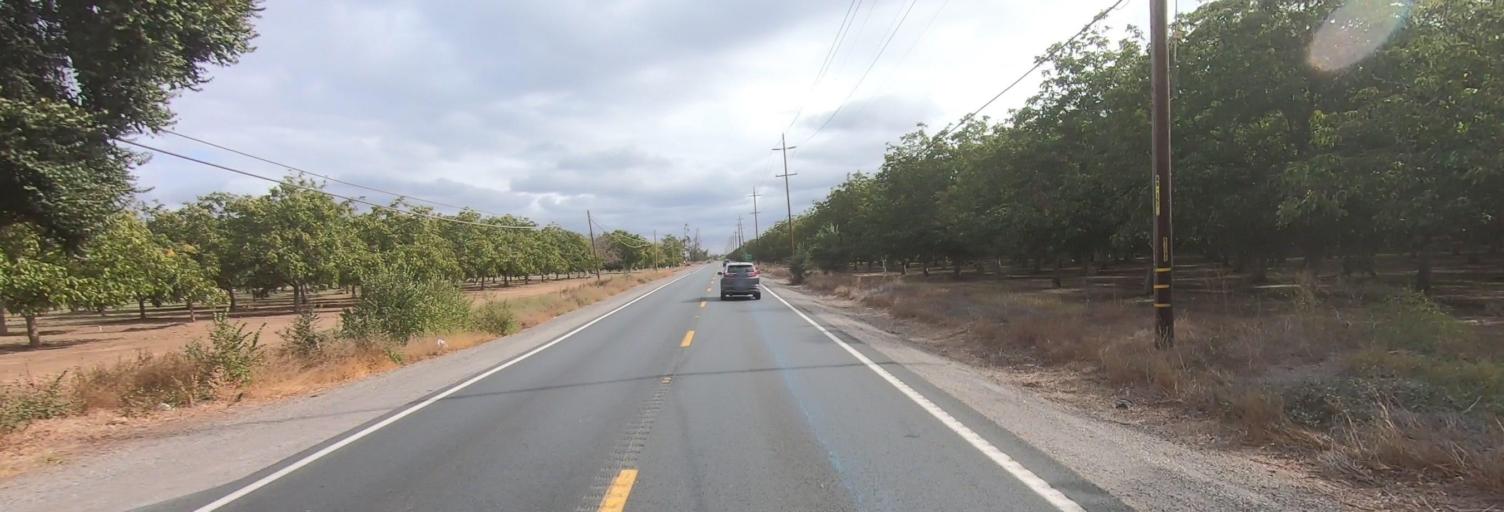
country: US
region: California
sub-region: San Joaquin County
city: Garden Acres
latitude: 37.9789
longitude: -121.2137
